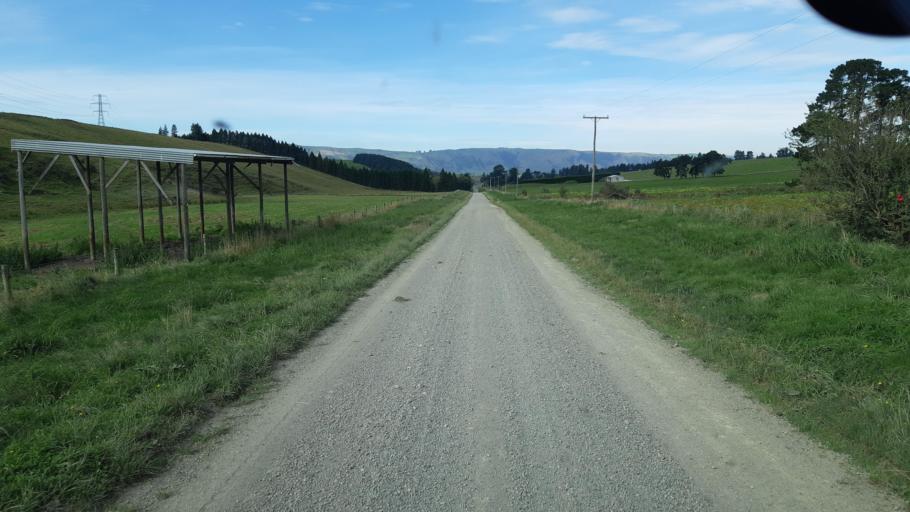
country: NZ
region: Canterbury
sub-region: Timaru District
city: Pleasant Point
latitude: -44.2094
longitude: 170.7992
